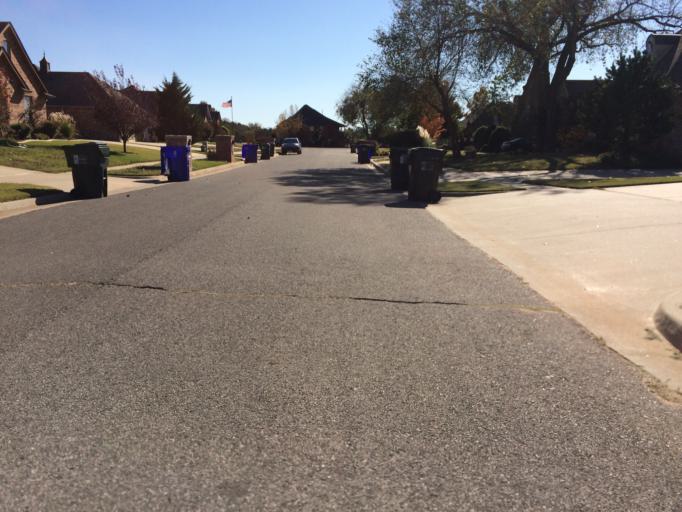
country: US
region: Oklahoma
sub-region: Cleveland County
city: Noble
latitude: 35.1658
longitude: -97.4198
